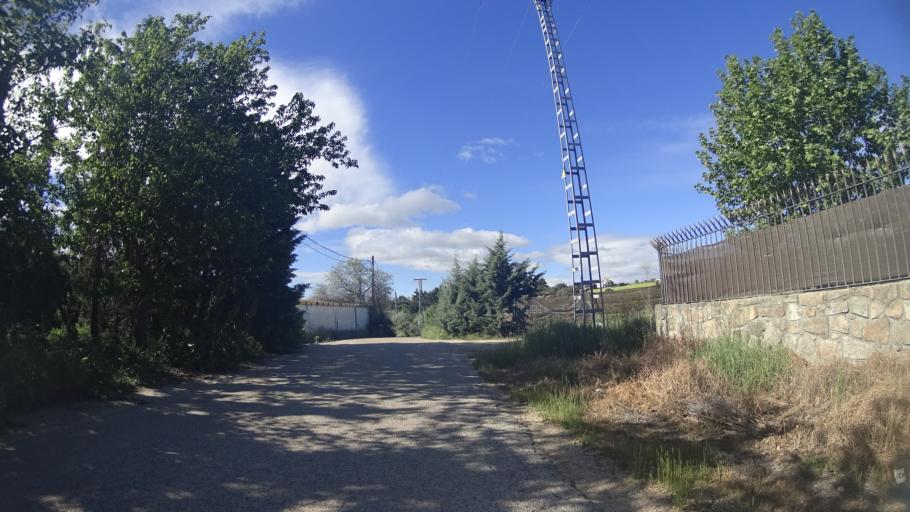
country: ES
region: Madrid
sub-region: Provincia de Madrid
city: Villanueva del Pardillo
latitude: 40.4963
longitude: -3.9406
